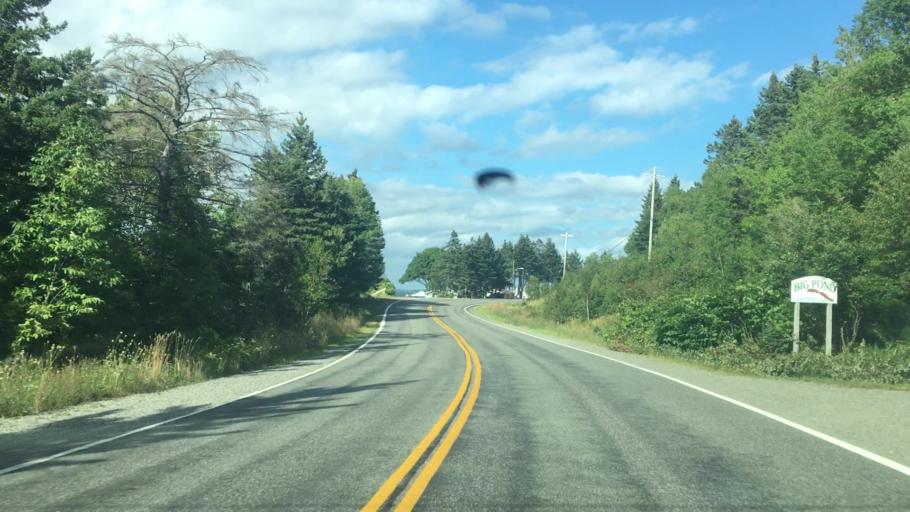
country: CA
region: Nova Scotia
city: Sydney
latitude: 45.8752
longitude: -60.6029
